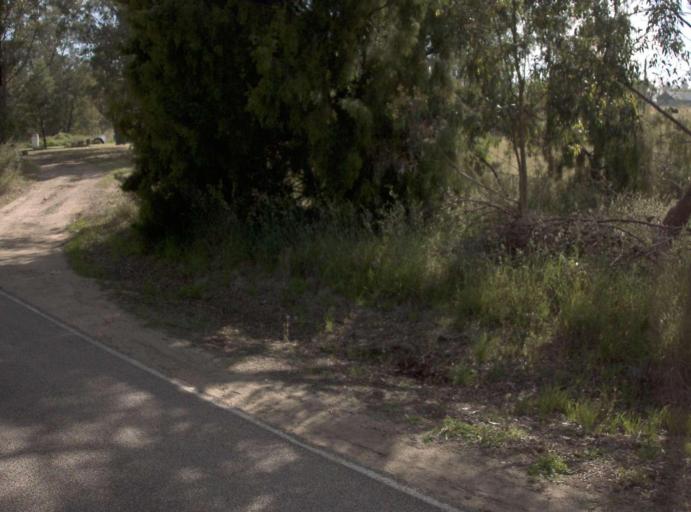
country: AU
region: Victoria
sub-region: East Gippsland
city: Lakes Entrance
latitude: -37.5300
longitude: 148.1541
